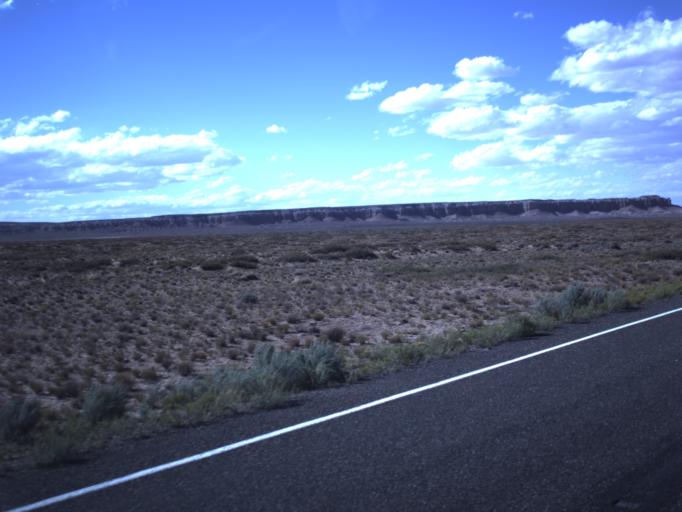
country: US
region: Utah
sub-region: Wayne County
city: Loa
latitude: 38.1863
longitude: -110.6274
